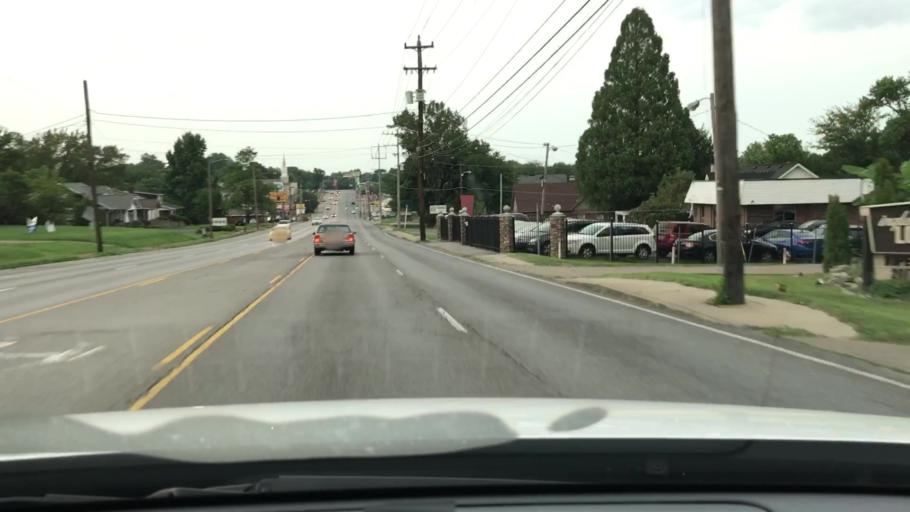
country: US
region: Tennessee
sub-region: Davidson County
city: Nashville
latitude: 36.2169
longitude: -86.7288
